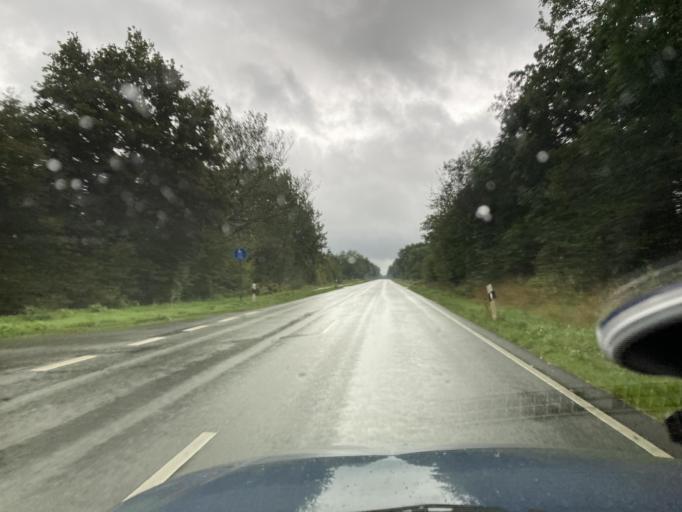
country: DE
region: Schleswig-Holstein
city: Suderdorf
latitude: 54.2184
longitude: 9.3608
